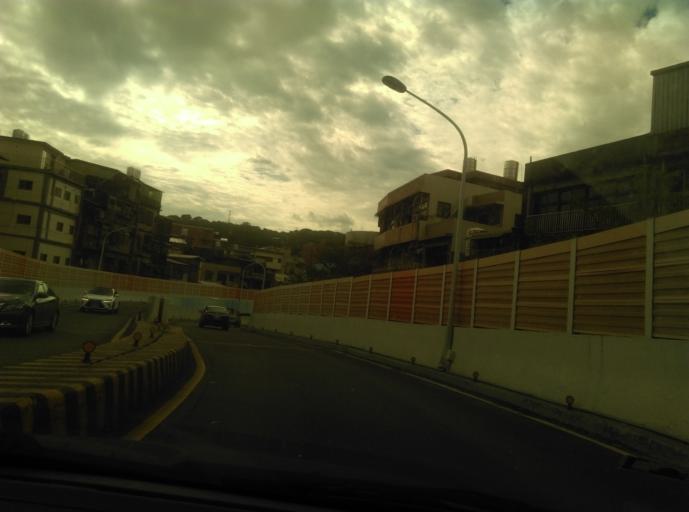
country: TW
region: Taiwan
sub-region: Keelung
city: Keelung
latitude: 25.1278
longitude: 121.7400
